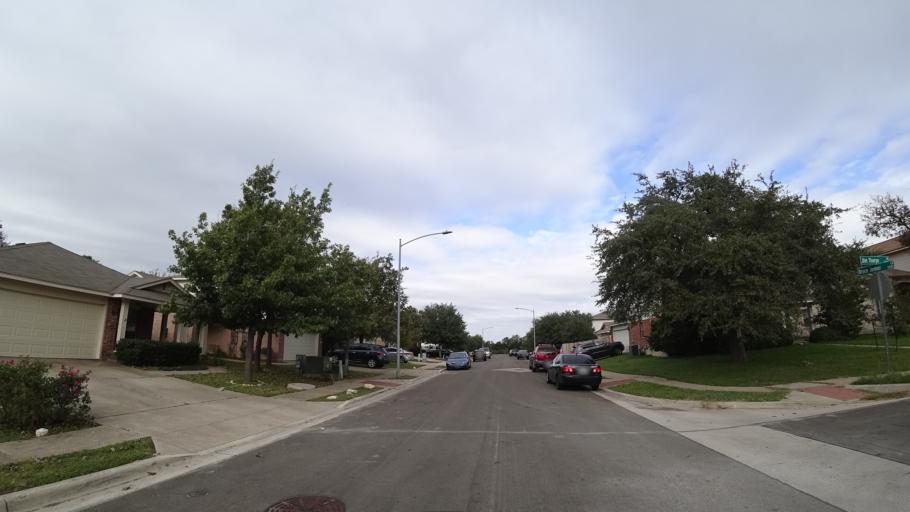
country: US
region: Texas
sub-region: Travis County
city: Manchaca
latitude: 30.1540
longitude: -97.8455
